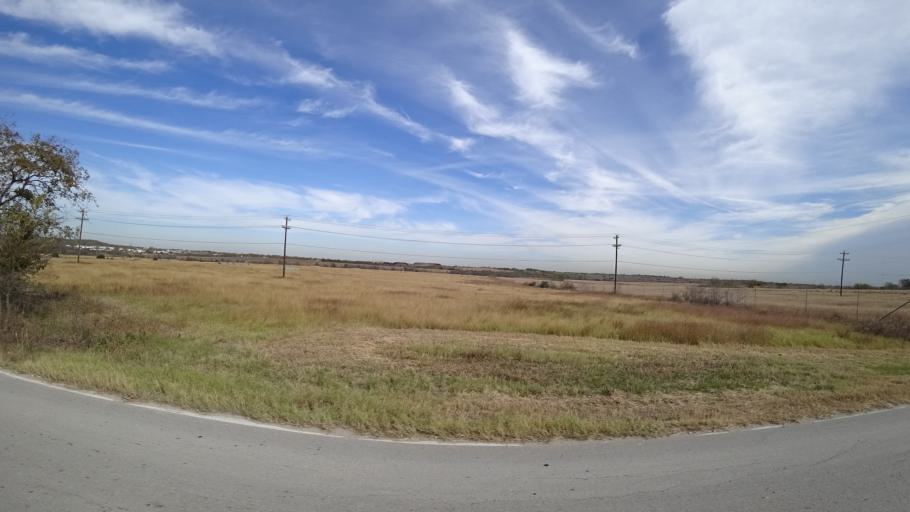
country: US
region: Texas
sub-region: Travis County
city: Onion Creek
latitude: 30.1424
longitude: -97.6929
